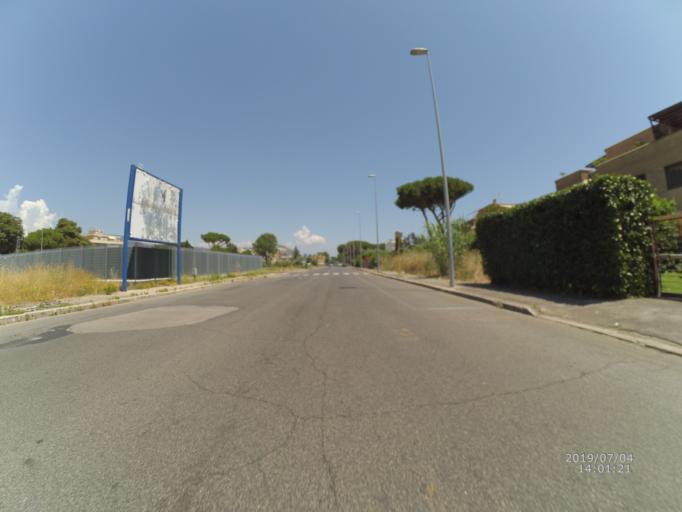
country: IT
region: Latium
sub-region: Provincia di Latina
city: Terracina
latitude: 41.2862
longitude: 13.2252
